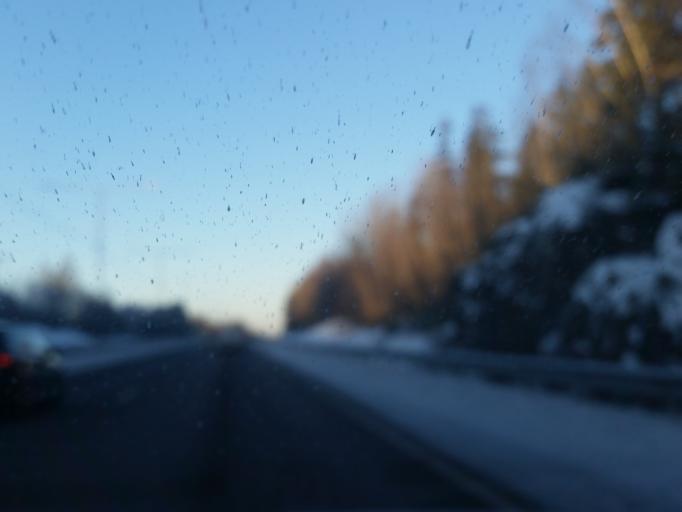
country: SE
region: Stockholm
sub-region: Sodertalje Kommun
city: Soedertaelje
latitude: 59.1797
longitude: 17.6060
